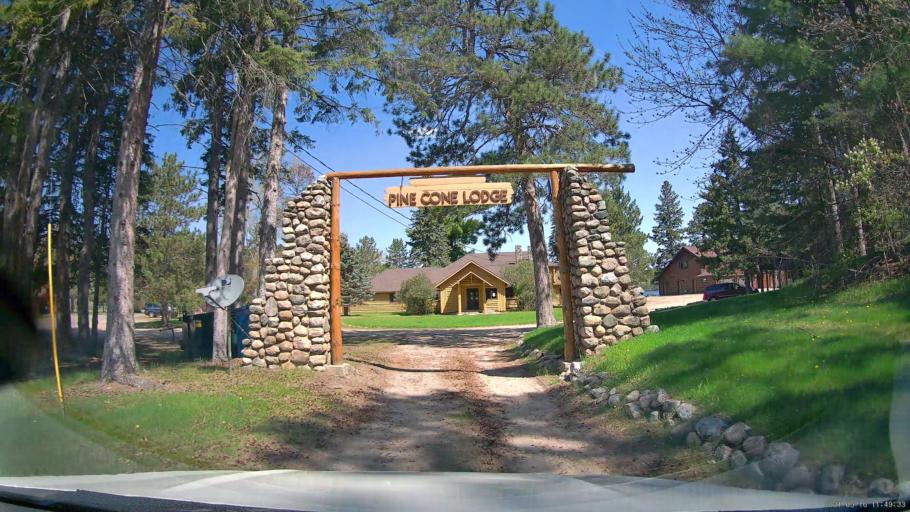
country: US
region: Minnesota
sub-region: Hubbard County
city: Park Rapids
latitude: 46.9873
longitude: -94.9520
